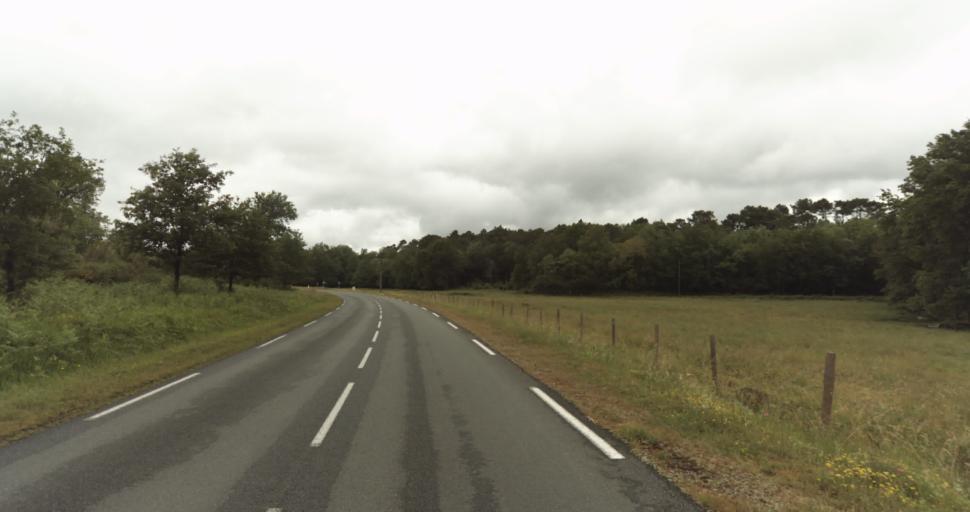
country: FR
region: Aquitaine
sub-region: Departement de la Dordogne
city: Belves
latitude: 44.6856
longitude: 0.9894
